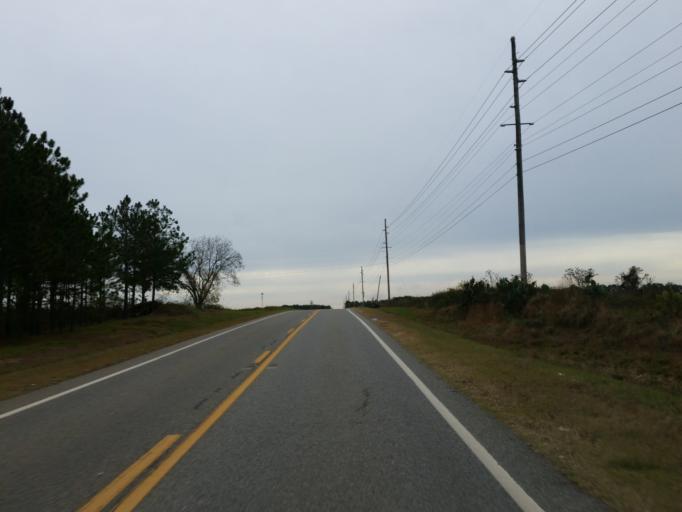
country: US
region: Georgia
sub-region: Crisp County
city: Cordele
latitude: 31.9135
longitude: -83.7086
